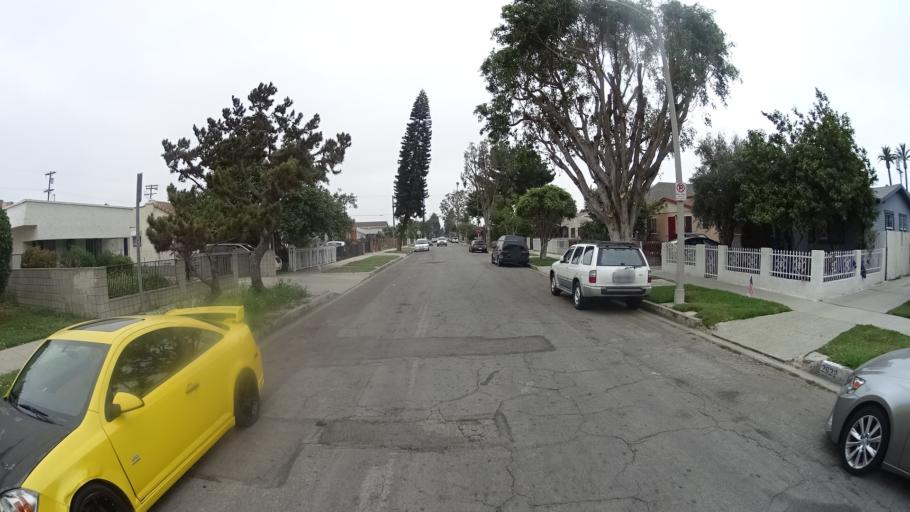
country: US
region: California
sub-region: Los Angeles County
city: View Park-Windsor Hills
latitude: 34.0277
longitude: -118.3521
